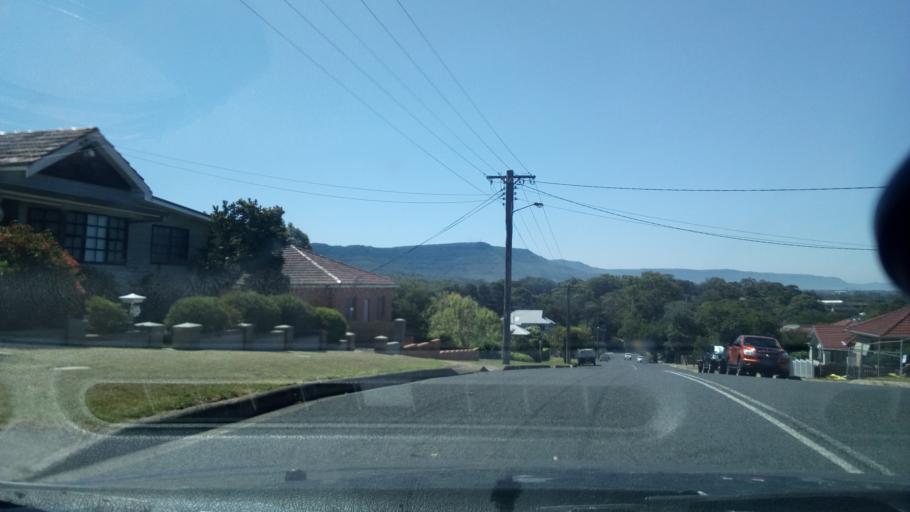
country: AU
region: New South Wales
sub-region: Wollongong
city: Gwynneville
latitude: -34.4225
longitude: 150.8779
